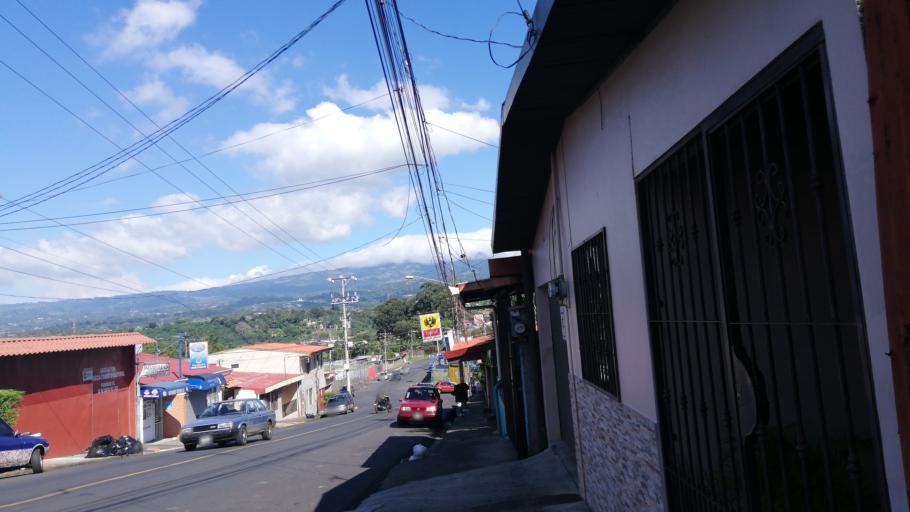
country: CR
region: Alajuela
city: San Juan
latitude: 10.0747
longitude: -84.3099
